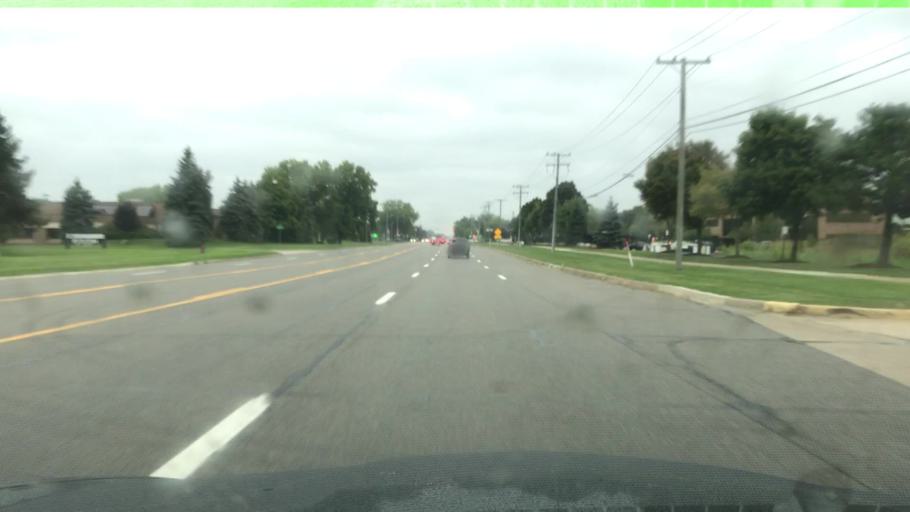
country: US
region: Michigan
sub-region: Oakland County
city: Clawson
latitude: 42.5457
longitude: -83.1075
